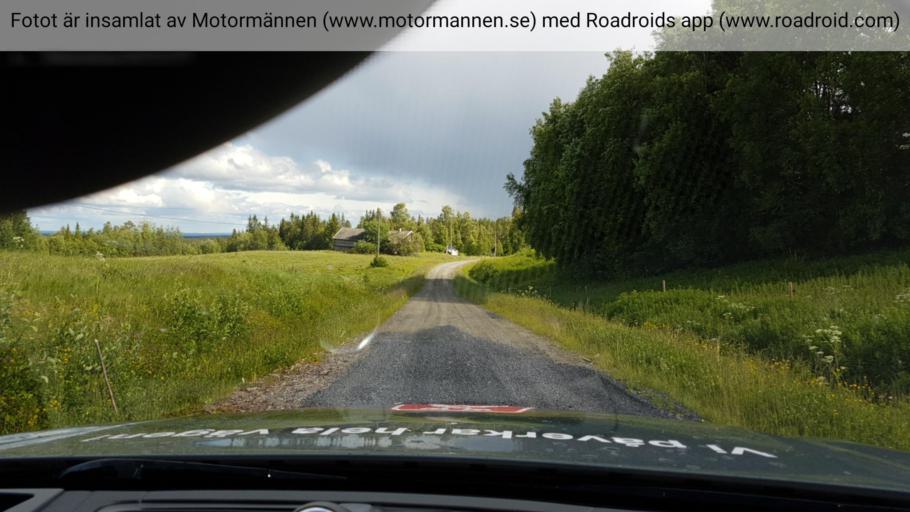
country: SE
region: Jaemtland
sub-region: Bergs Kommun
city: Hoverberg
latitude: 63.0335
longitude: 14.0672
